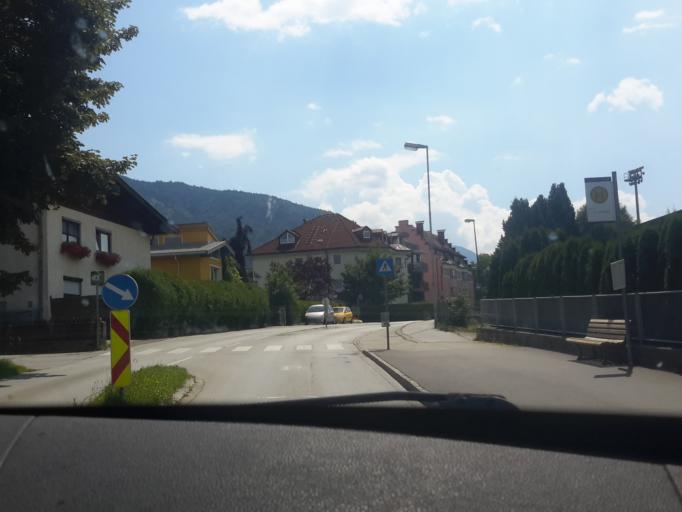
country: AT
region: Tyrol
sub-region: Politischer Bezirk Kufstein
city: Kufstein
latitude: 47.5885
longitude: 12.1709
